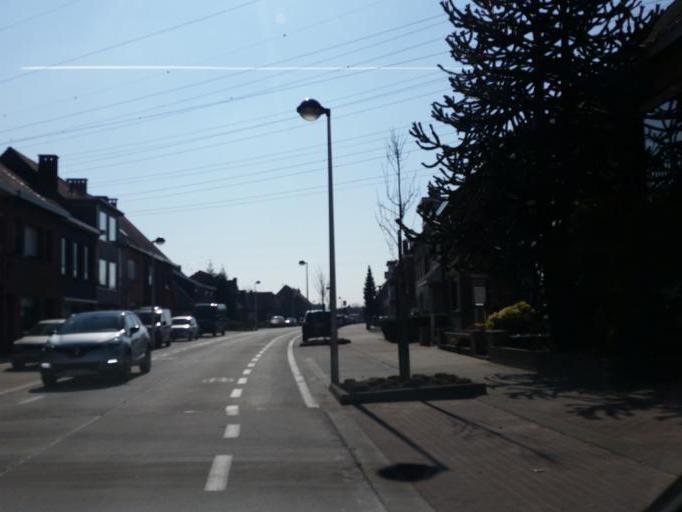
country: BE
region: Flanders
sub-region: Provincie Oost-Vlaanderen
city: Kruibeke
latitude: 51.1379
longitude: 4.2945
